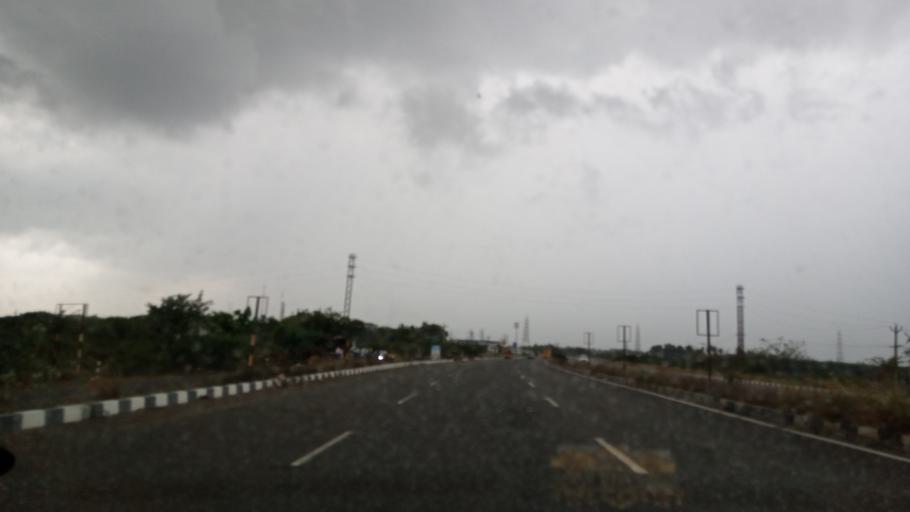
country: IN
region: Tamil Nadu
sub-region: Kancheepuram
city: Sriperumbudur
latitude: 12.9336
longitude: 79.9342
